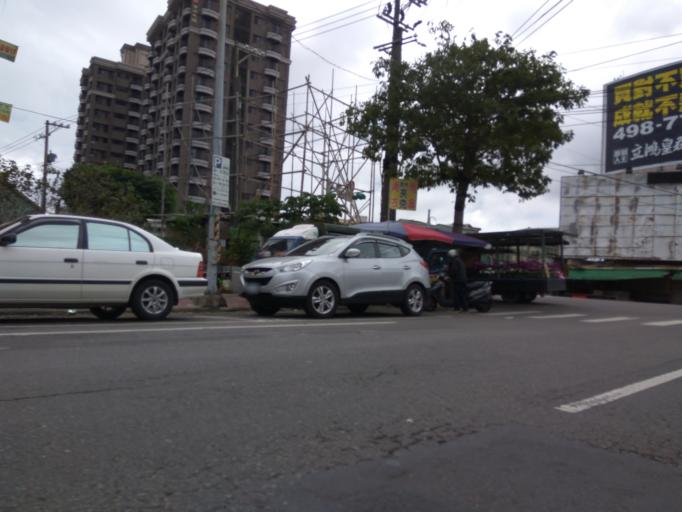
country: TW
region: Taiwan
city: Taoyuan City
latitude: 24.9603
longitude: 121.2101
